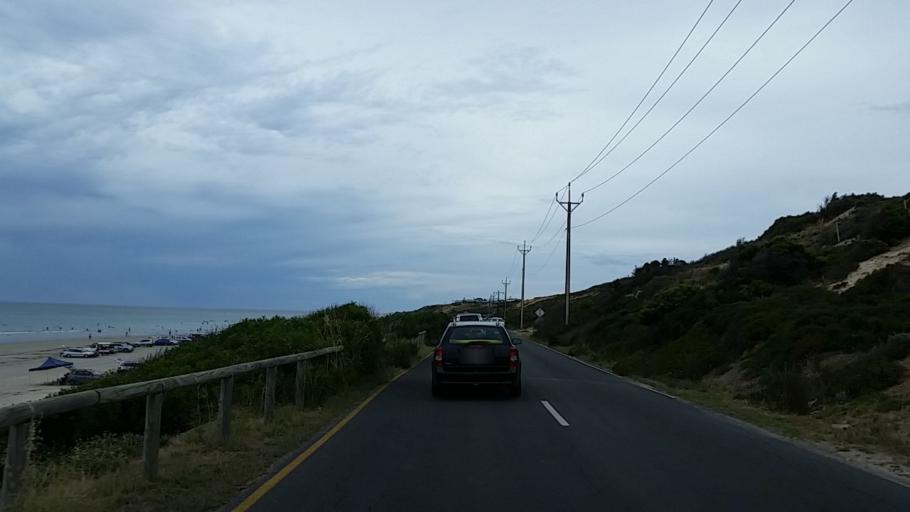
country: AU
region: South Australia
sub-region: Onkaparinga
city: Port Willunga
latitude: -35.2937
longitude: 138.4459
